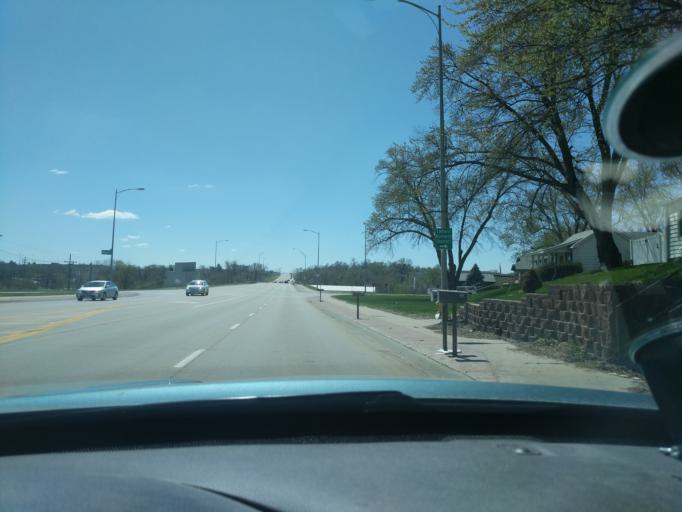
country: US
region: Nebraska
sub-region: Douglas County
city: Elkhorn
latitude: 41.2839
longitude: -96.2345
